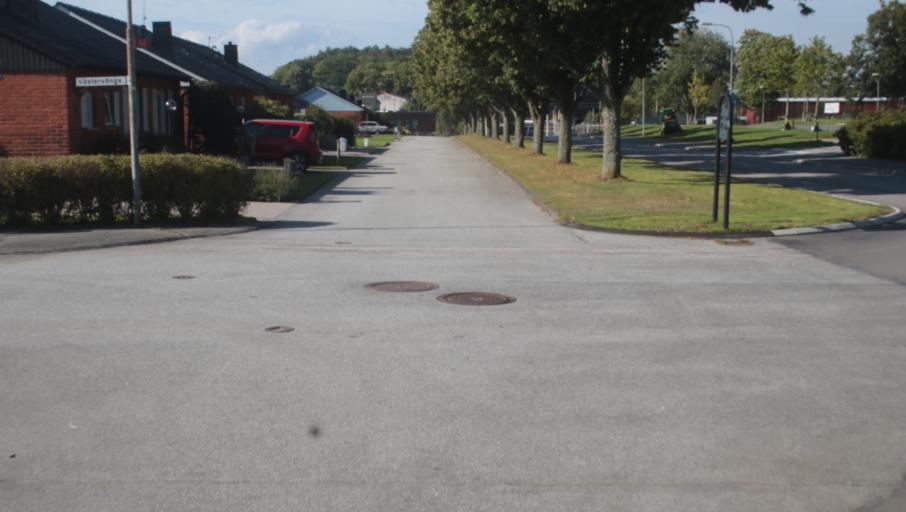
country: SE
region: Blekinge
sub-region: Karlshamns Kommun
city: Karlshamn
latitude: 56.1758
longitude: 14.8497
